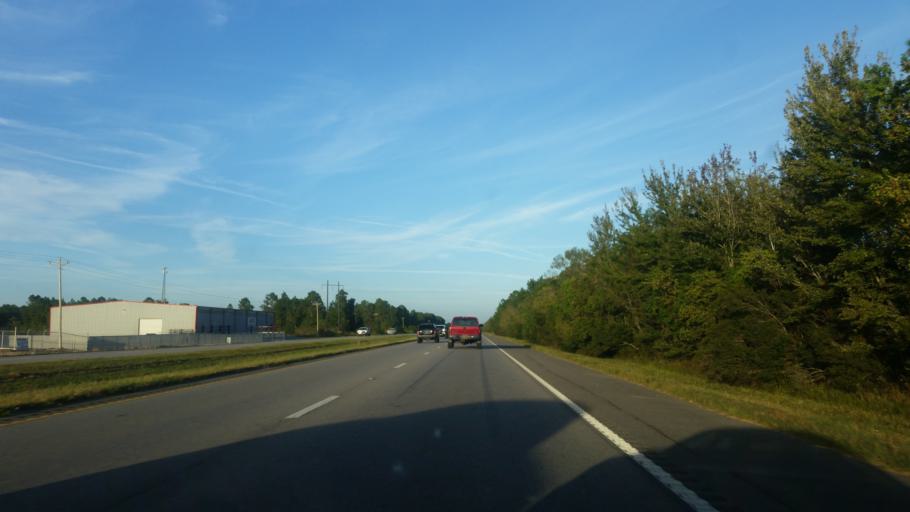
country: US
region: Mississippi
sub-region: Jackson County
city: Moss Point
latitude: 30.4095
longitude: -88.4772
